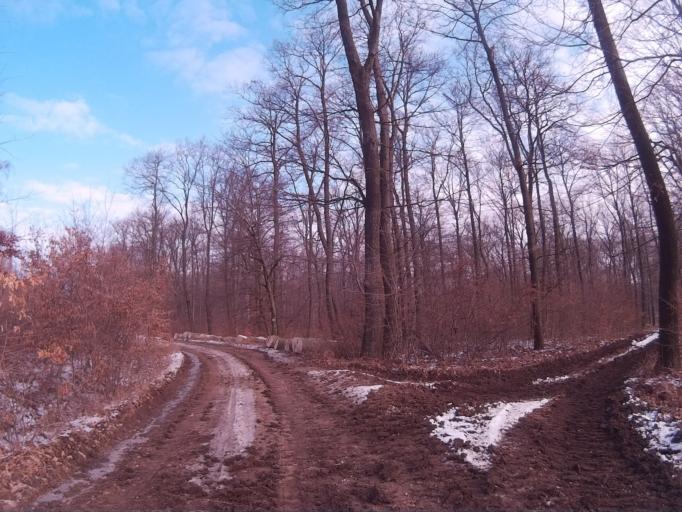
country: HU
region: Komarom-Esztergom
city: Labatlan
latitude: 47.6826
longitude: 18.5087
